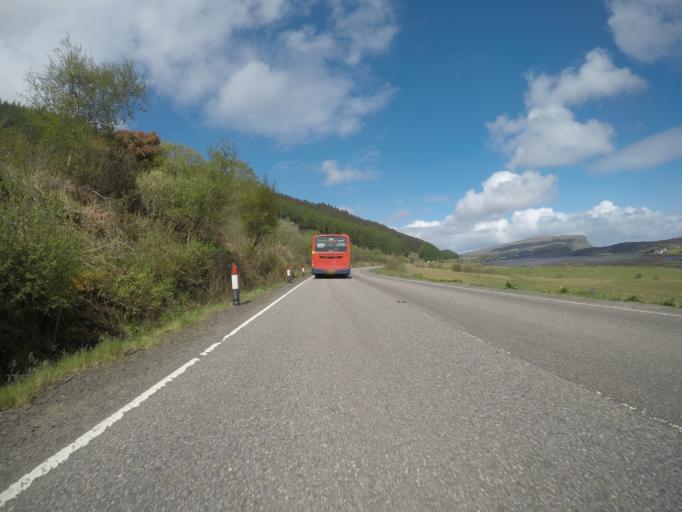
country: GB
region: Scotland
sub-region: Highland
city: Portree
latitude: 57.3900
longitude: -6.2051
